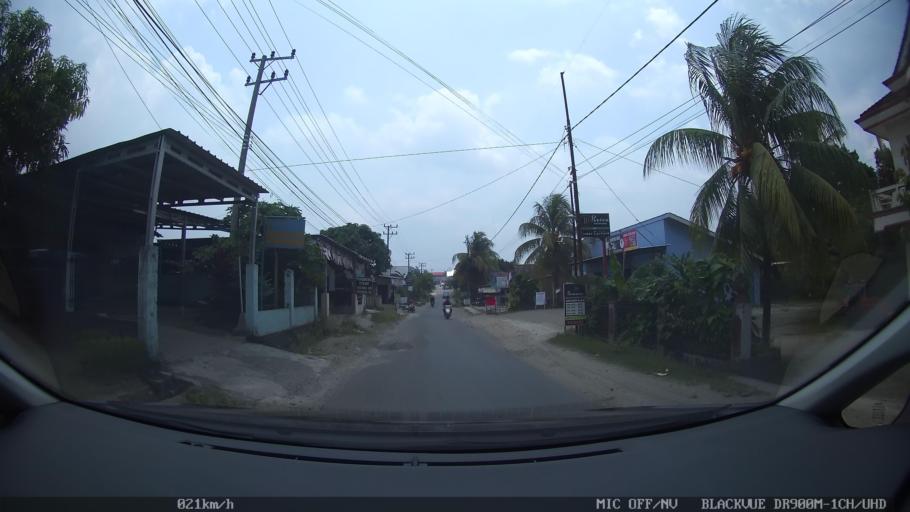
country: ID
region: Lampung
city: Pringsewu
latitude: -5.3502
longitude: 104.9725
